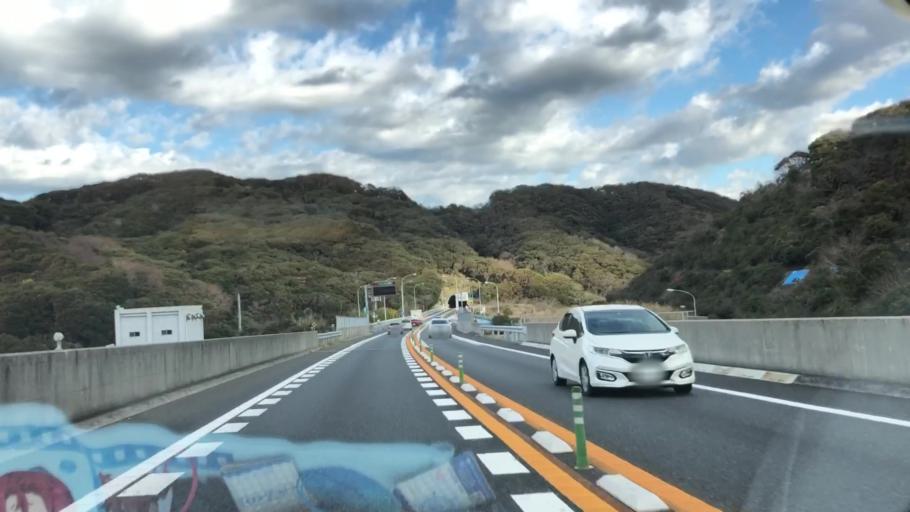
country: JP
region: Chiba
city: Futtsu
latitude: 35.1705
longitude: 139.8303
